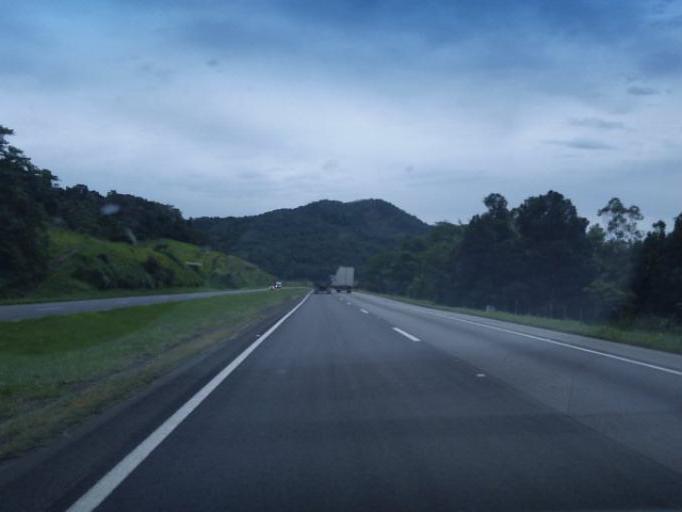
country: BR
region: Sao Paulo
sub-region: Juquia
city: Juquia
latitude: -24.3537
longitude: -47.6599
